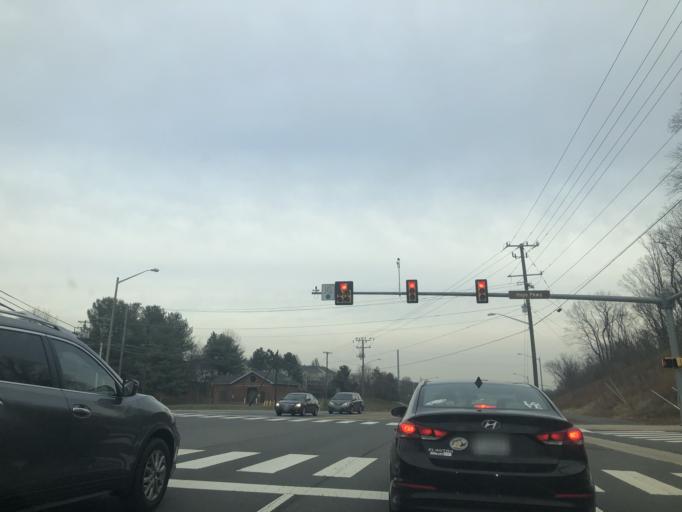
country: US
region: Virginia
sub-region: Loudoun County
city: Leesburg
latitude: 39.0954
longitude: -77.5534
